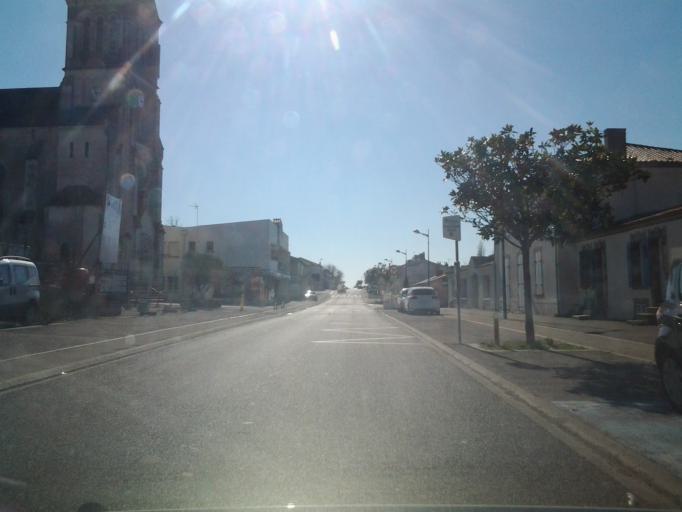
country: FR
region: Pays de la Loire
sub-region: Departement de la Vendee
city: Saint-Mathurin
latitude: 46.5653
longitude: -1.7139
